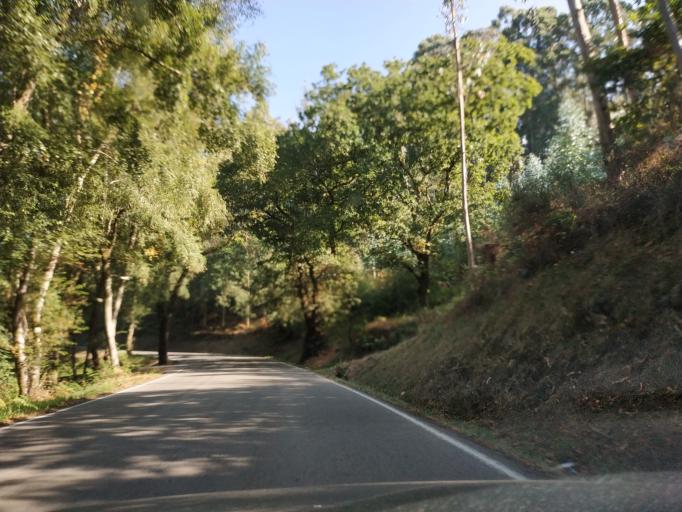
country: ES
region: Galicia
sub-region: Provincia da Coruna
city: Cerceda
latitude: 43.2335
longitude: -8.4707
